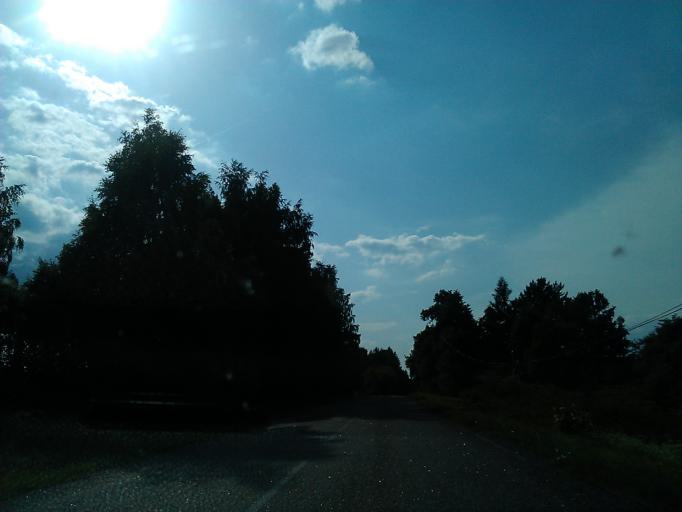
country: LV
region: Skrunda
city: Skrunda
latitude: 56.6911
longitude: 21.8687
